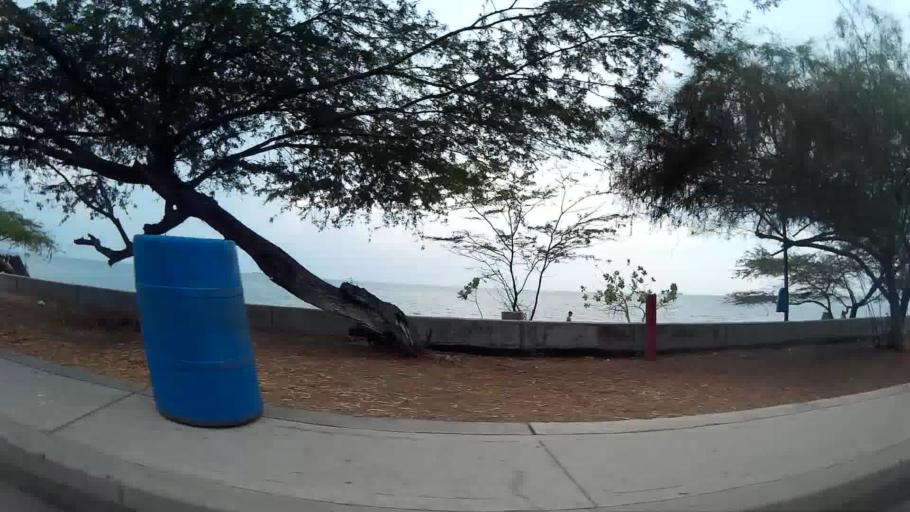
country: CO
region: Magdalena
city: Cienaga
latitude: 11.1190
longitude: -74.2323
